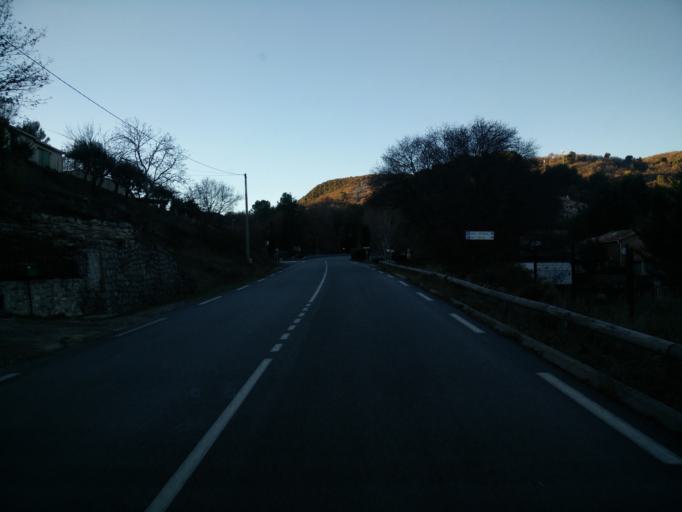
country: FR
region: Provence-Alpes-Cote d'Azur
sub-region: Departement du Var
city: Montferrat
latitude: 43.6109
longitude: 6.4807
